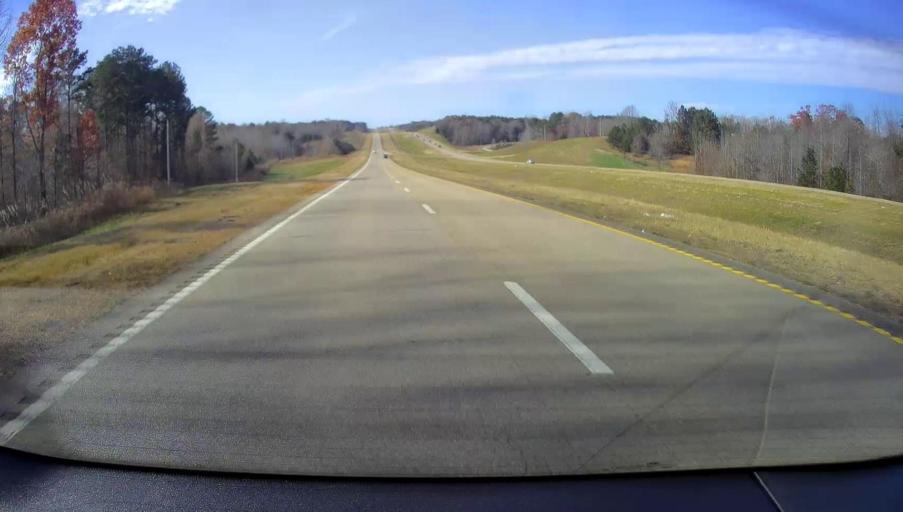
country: US
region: Mississippi
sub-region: Tippah County
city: Ripley
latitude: 34.9551
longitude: -88.9658
